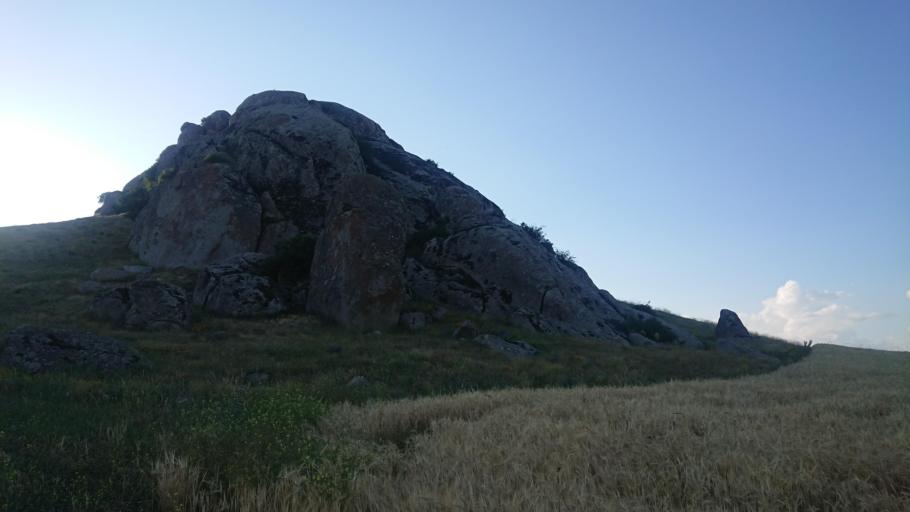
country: TR
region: Aksaray
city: Agacoren
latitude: 38.8329
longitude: 33.8837
